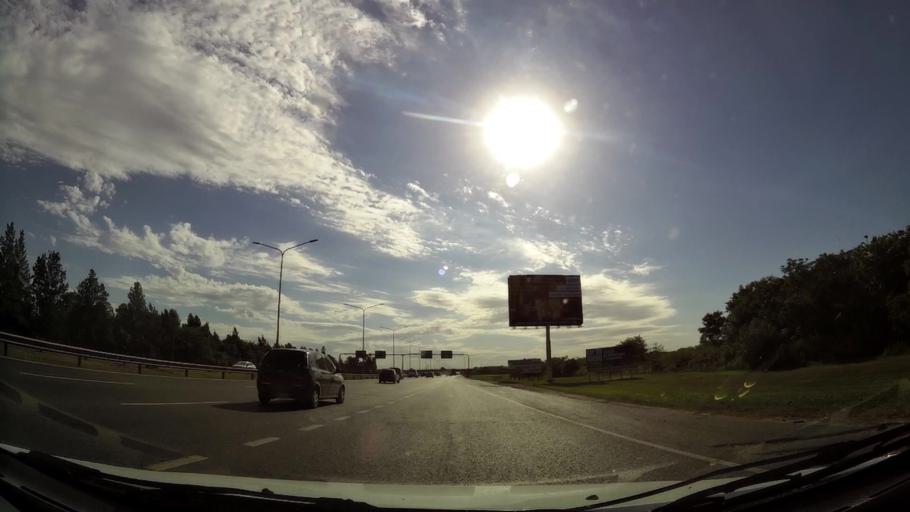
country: AR
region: Buenos Aires
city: Hurlingham
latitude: -34.5660
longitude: -58.6343
